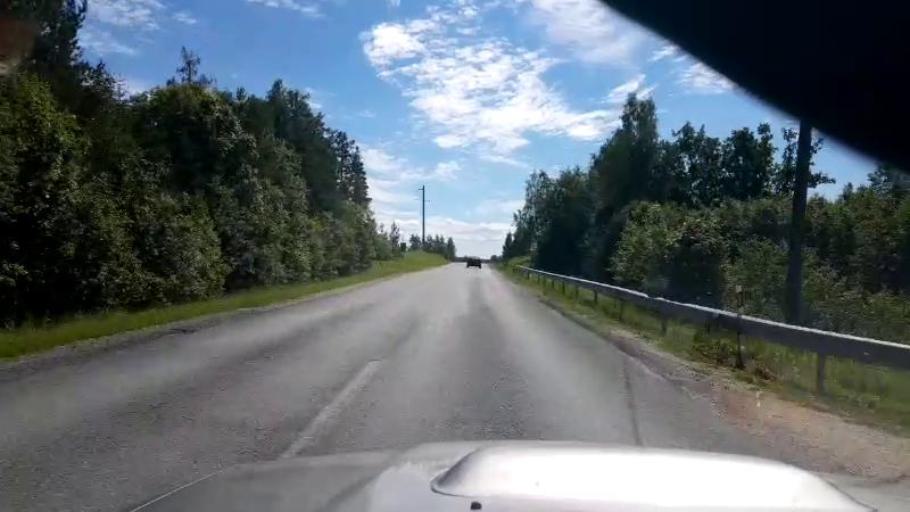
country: EE
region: Jogevamaa
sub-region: Jogeva linn
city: Jogeva
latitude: 58.8397
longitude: 26.2906
